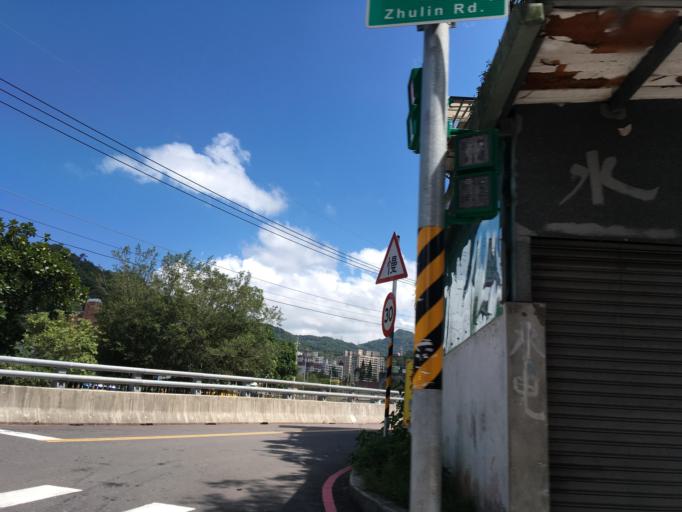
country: TW
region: Taipei
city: Taipei
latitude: 24.9513
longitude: 121.5537
